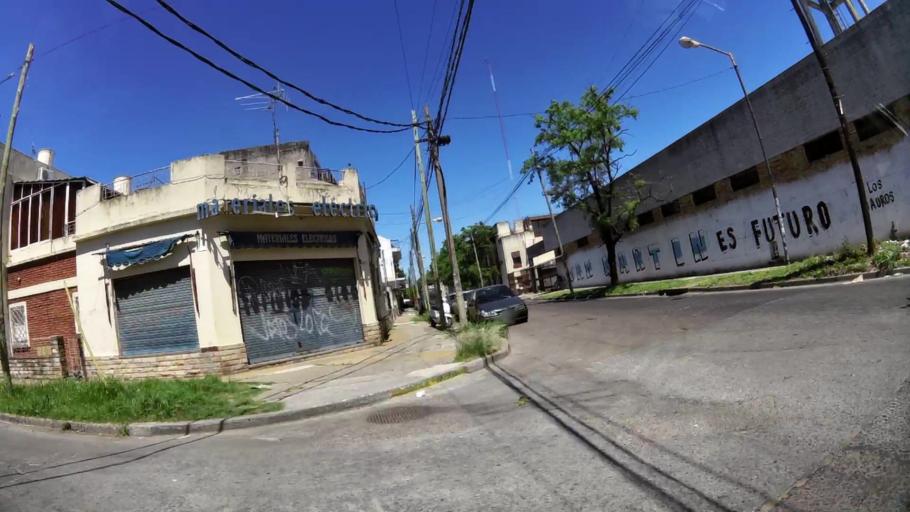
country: AR
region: Buenos Aires
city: Caseros
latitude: -34.5746
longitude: -58.5608
